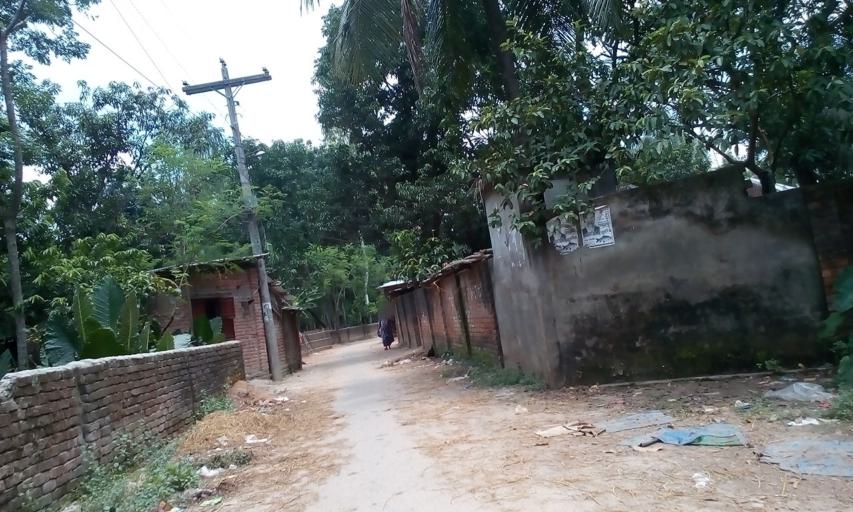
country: IN
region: West Bengal
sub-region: Dakshin Dinajpur
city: Balurghat
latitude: 25.3837
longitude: 88.9962
